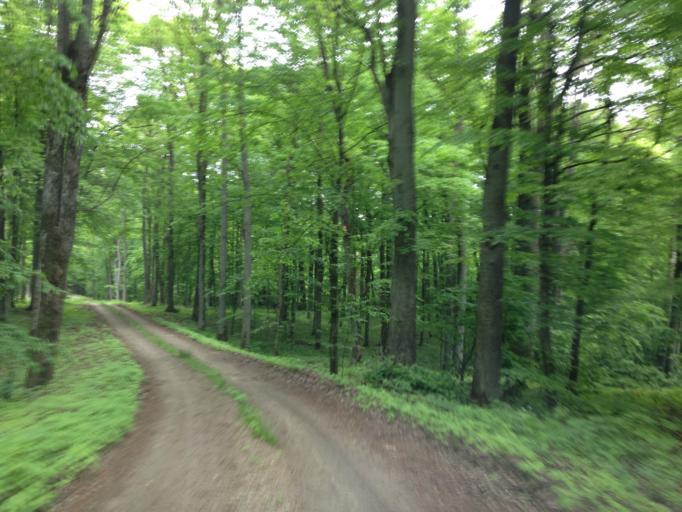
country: PL
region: Kujawsko-Pomorskie
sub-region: Powiat brodnicki
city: Gorzno
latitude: 53.2536
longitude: 19.7173
